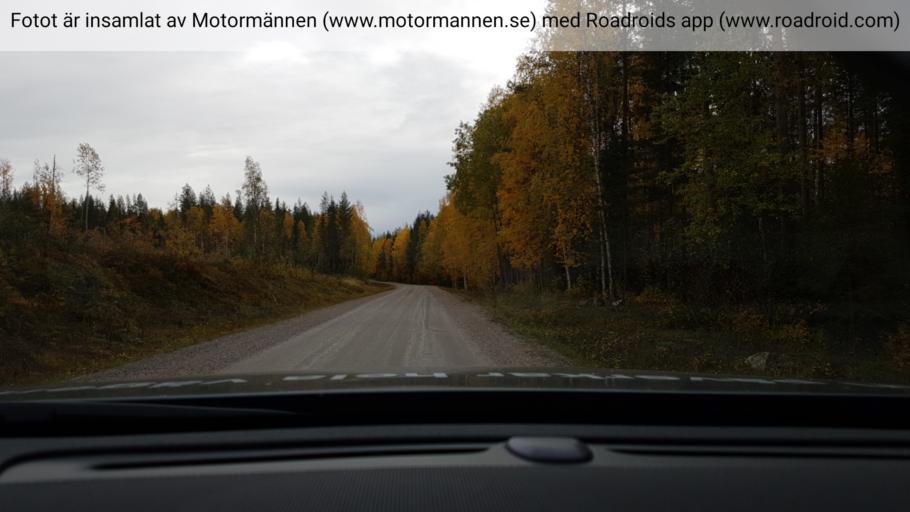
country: SE
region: Norrbotten
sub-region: Overkalix Kommun
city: OEverkalix
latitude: 66.2828
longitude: 22.9765
